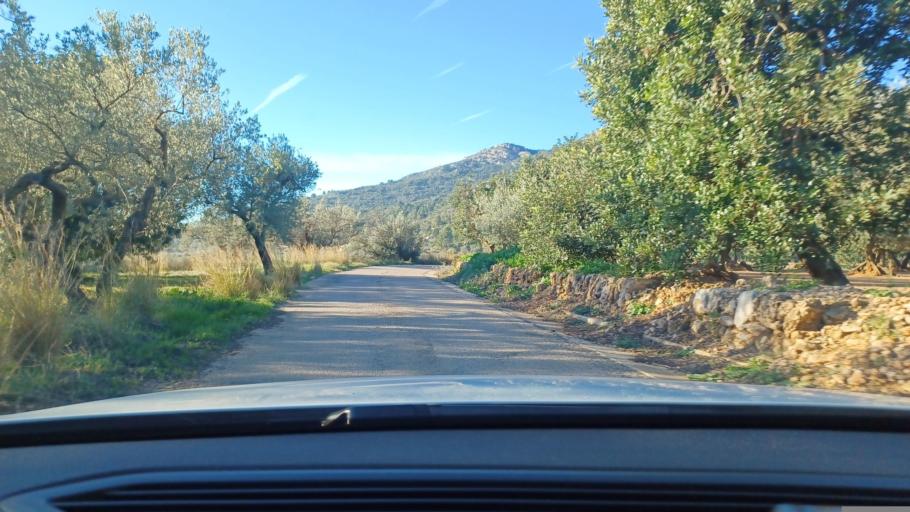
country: ES
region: Catalonia
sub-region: Provincia de Tarragona
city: Mas de Barberans
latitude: 40.7171
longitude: 0.3549
